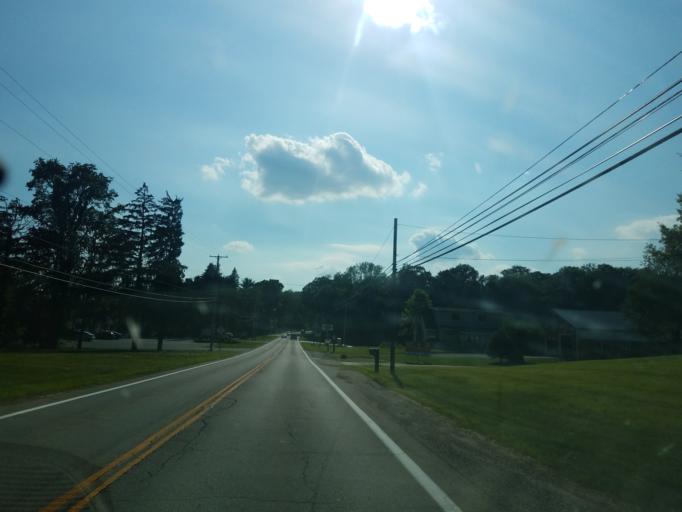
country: US
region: Ohio
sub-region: Stark County
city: Uniontown
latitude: 40.9770
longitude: -81.3943
